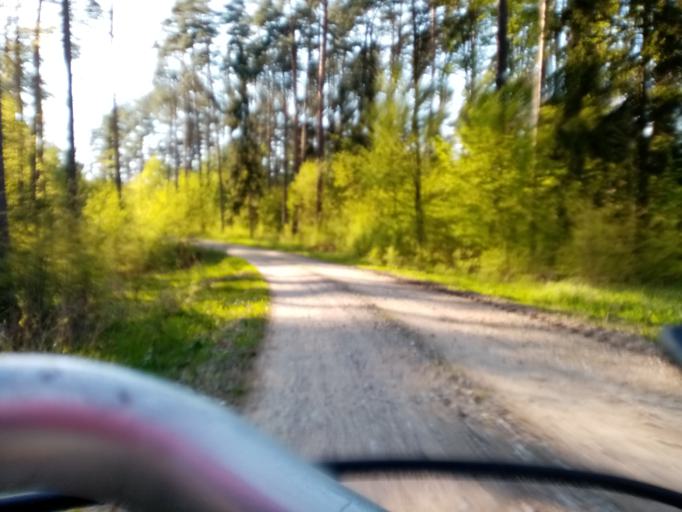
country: PL
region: Kujawsko-Pomorskie
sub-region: Powiat brodnicki
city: Gorzno
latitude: 53.1613
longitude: 19.6834
